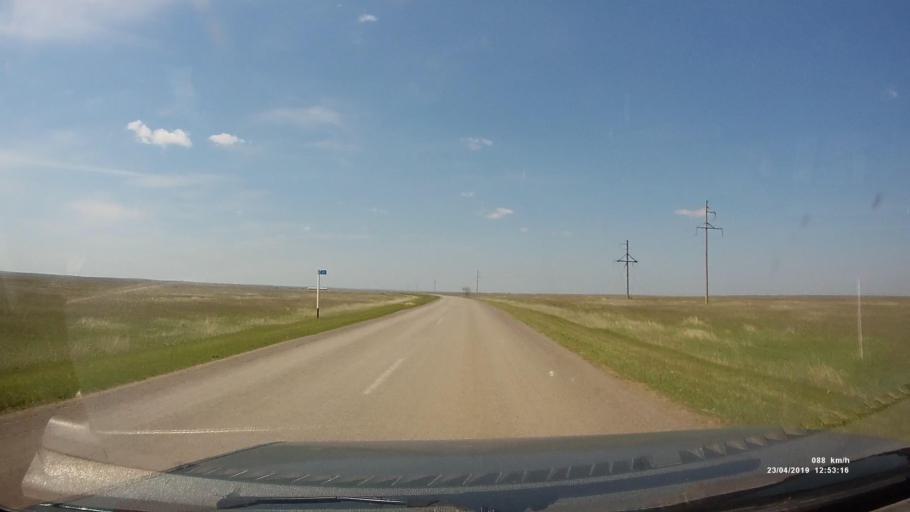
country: RU
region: Kalmykiya
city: Yashalta
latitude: 46.5725
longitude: 42.5983
